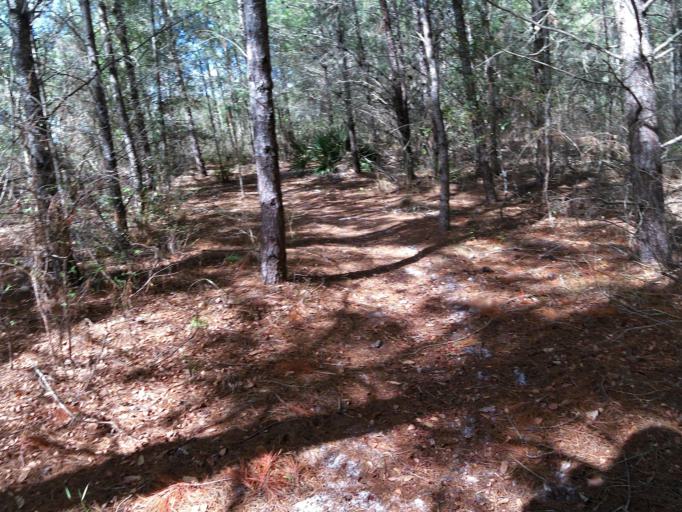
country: US
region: Florida
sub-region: Putnam County
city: Interlachen
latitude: 29.7694
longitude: -81.8672
